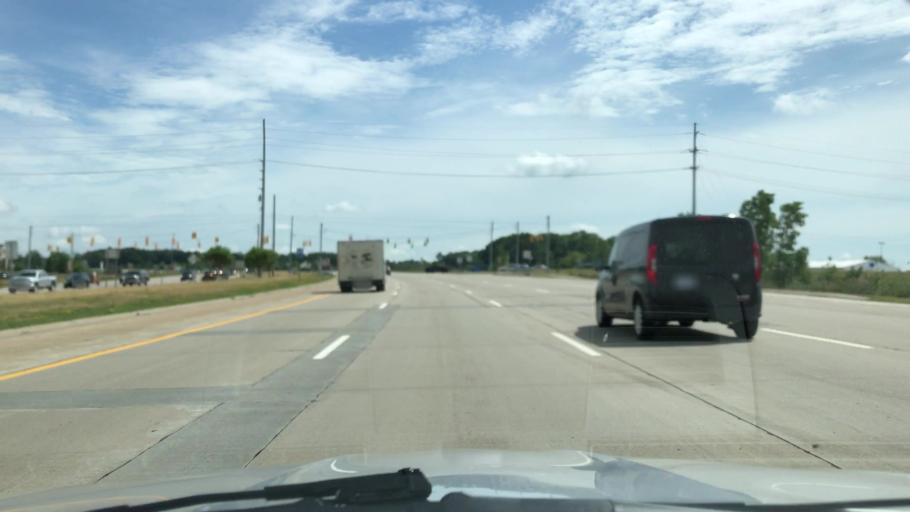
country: US
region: Michigan
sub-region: Oakland County
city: Wolverine Lake
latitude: 42.5428
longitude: -83.4519
